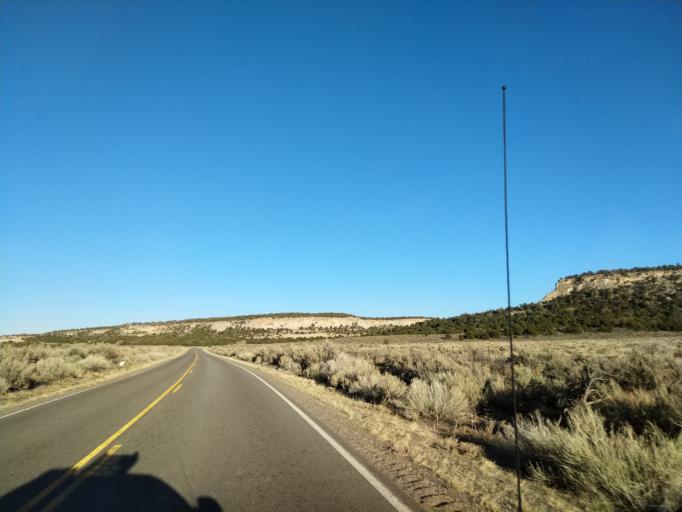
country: US
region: Colorado
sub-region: Mesa County
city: Fruita
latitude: 38.9835
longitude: -108.8067
